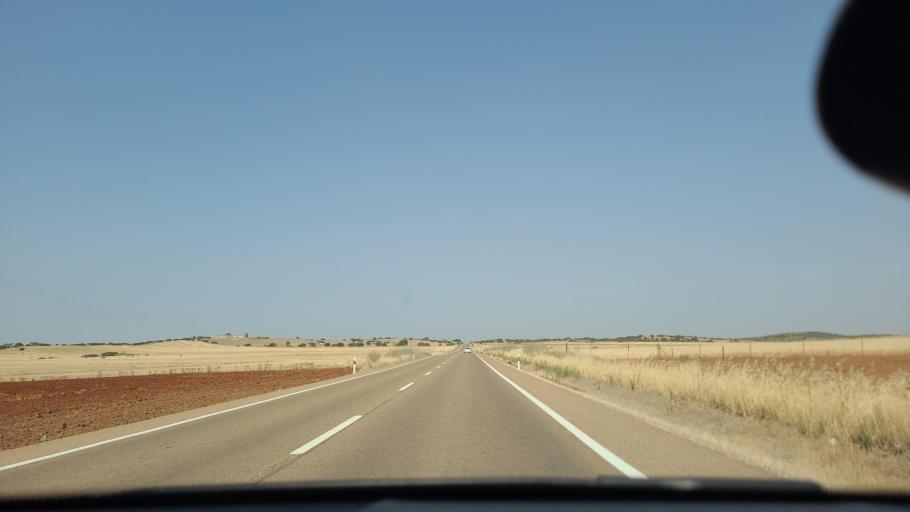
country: ES
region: Extremadura
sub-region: Provincia de Badajoz
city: Usagre
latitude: 38.3588
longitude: -6.2143
